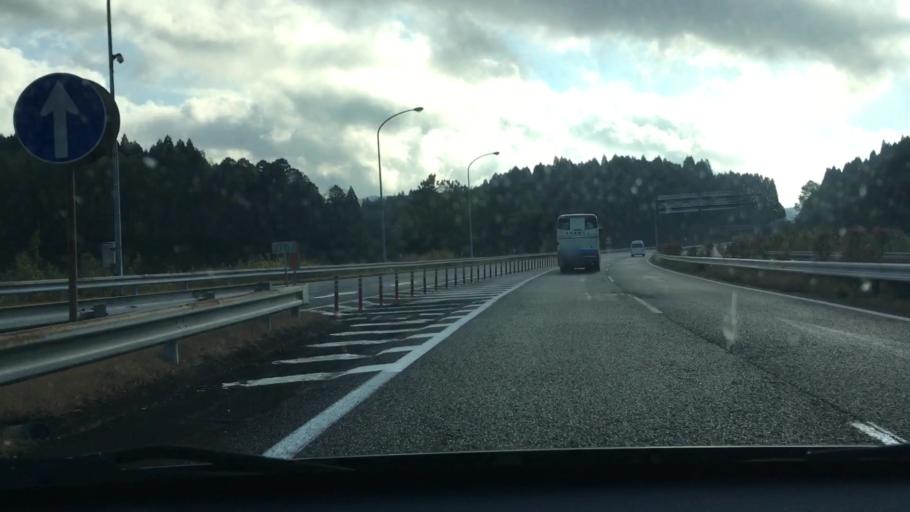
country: JP
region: Kagoshima
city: Okuchi-shinohara
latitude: 32.0284
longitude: 130.7965
